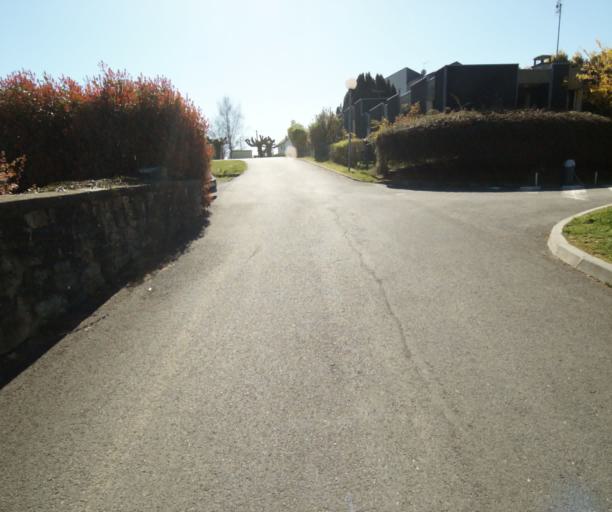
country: FR
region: Limousin
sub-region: Departement de la Correze
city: Seilhac
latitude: 45.3654
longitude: 1.7153
